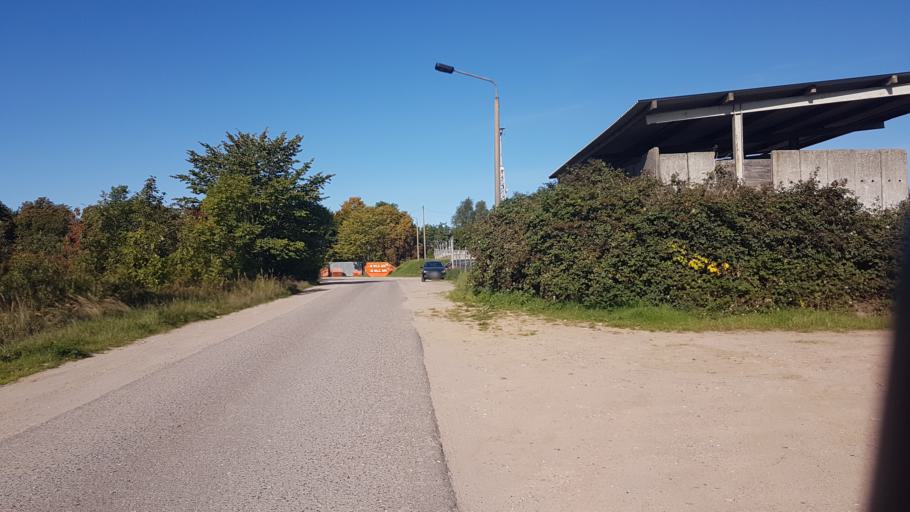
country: DE
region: Mecklenburg-Vorpommern
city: Sagard
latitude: 54.5012
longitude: 13.5373
